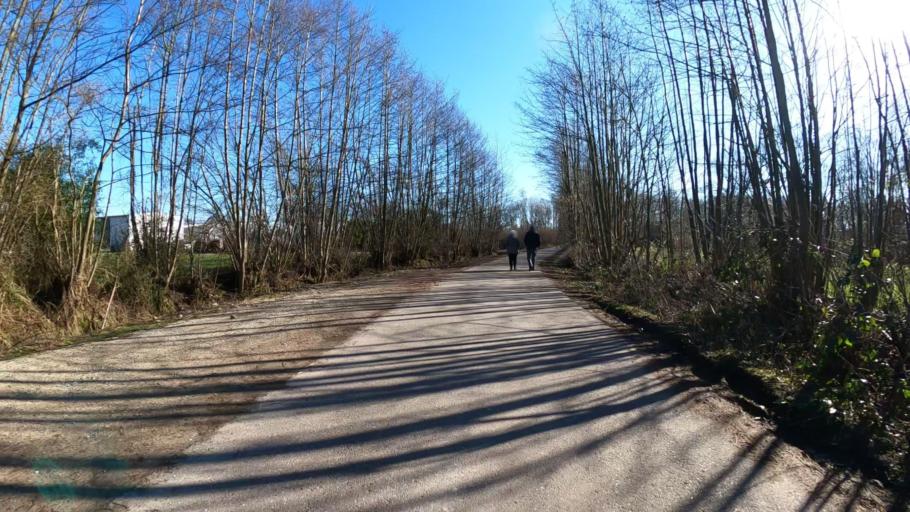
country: DE
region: Schleswig-Holstein
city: Kummerfeld
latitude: 53.6842
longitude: 9.7776
